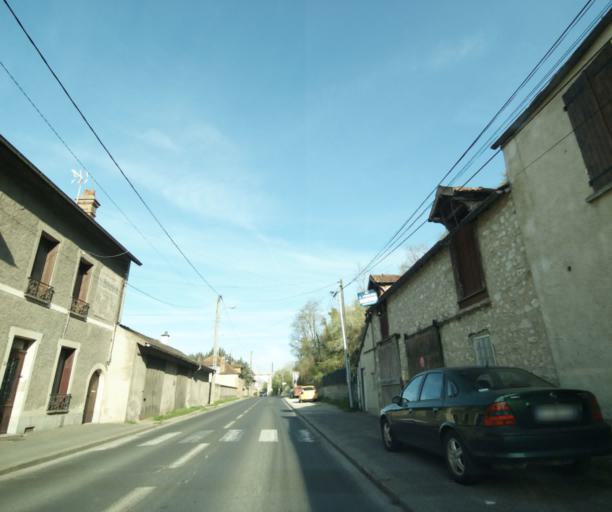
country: FR
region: Ile-de-France
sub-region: Departement de Seine-et-Marne
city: Saint-Mammes
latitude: 48.3793
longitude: 2.8167
